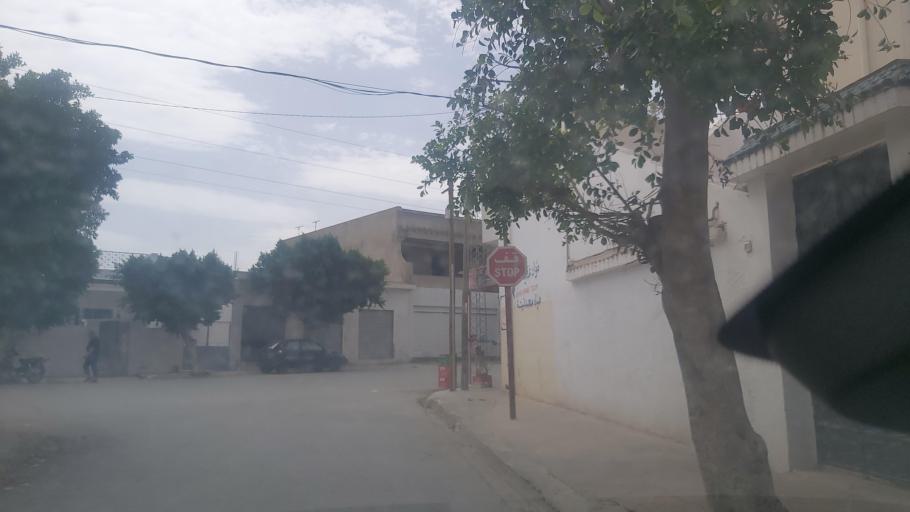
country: TN
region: Silyanah
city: Bu `Aradah
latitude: 36.3511
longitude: 9.6214
